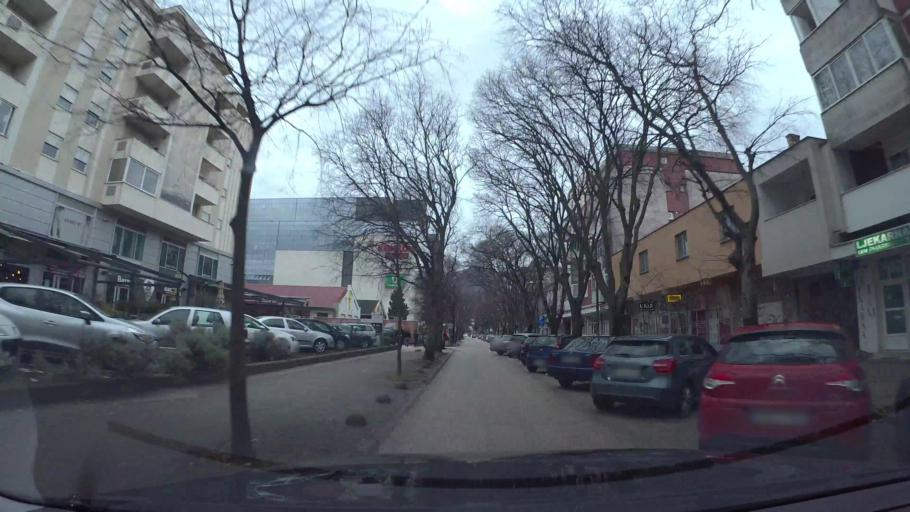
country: BA
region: Federation of Bosnia and Herzegovina
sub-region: Hercegovacko-Bosanski Kanton
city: Mostar
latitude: 43.3498
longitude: 17.8040
